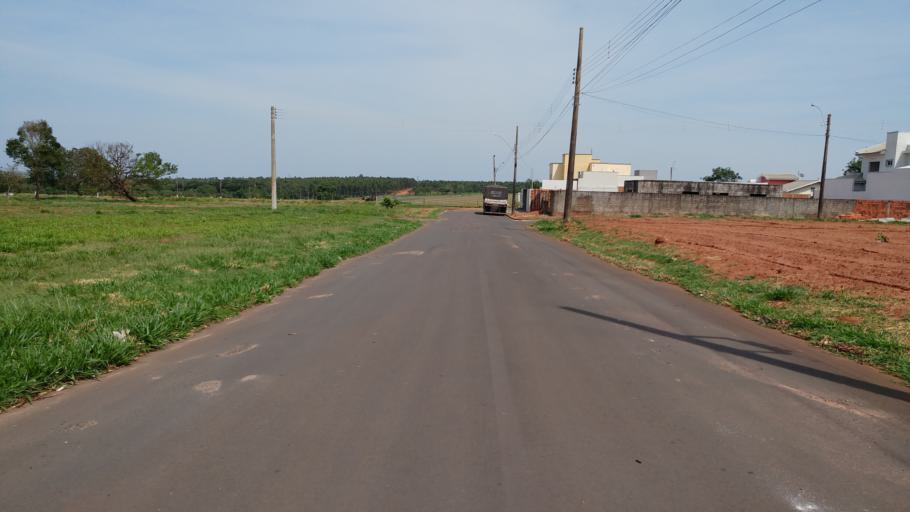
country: BR
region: Sao Paulo
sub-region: Paraguacu Paulista
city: Paraguacu Paulista
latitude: -22.4094
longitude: -50.5915
